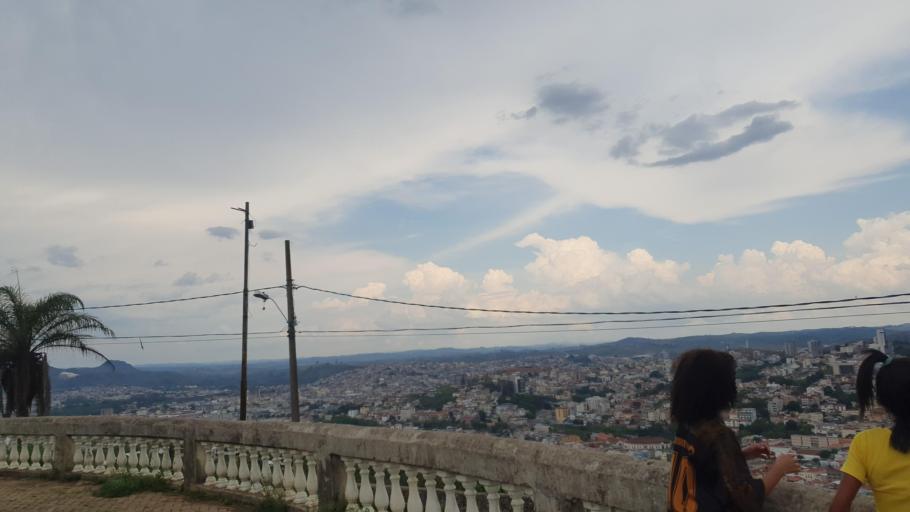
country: BR
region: Minas Gerais
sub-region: Sao Joao Del Rei
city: Sao Joao del Rei
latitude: -21.1282
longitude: -44.2615
